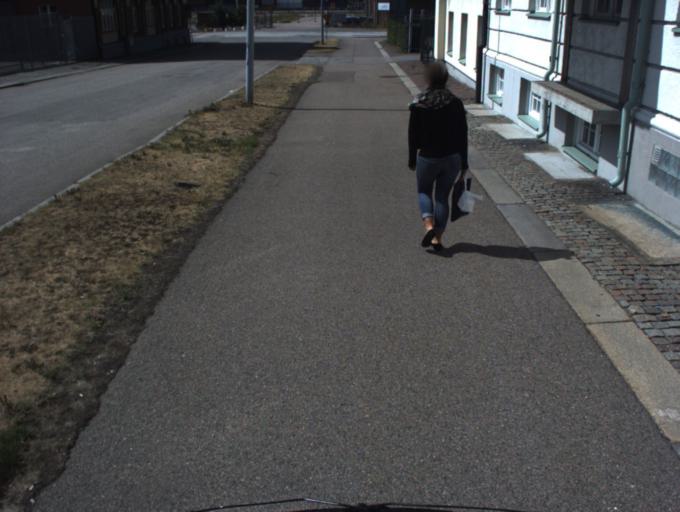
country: SE
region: Skane
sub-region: Helsingborg
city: Helsingborg
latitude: 56.0365
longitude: 12.7007
